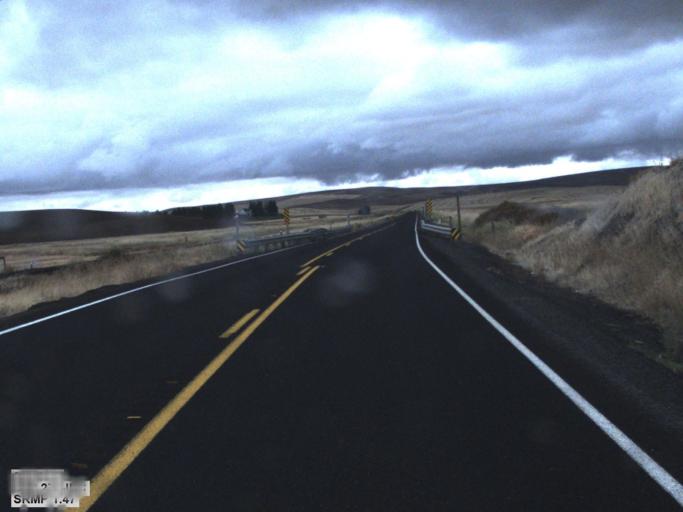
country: US
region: Washington
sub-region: Whitman County
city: Colfax
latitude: 47.1516
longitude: -117.2612
